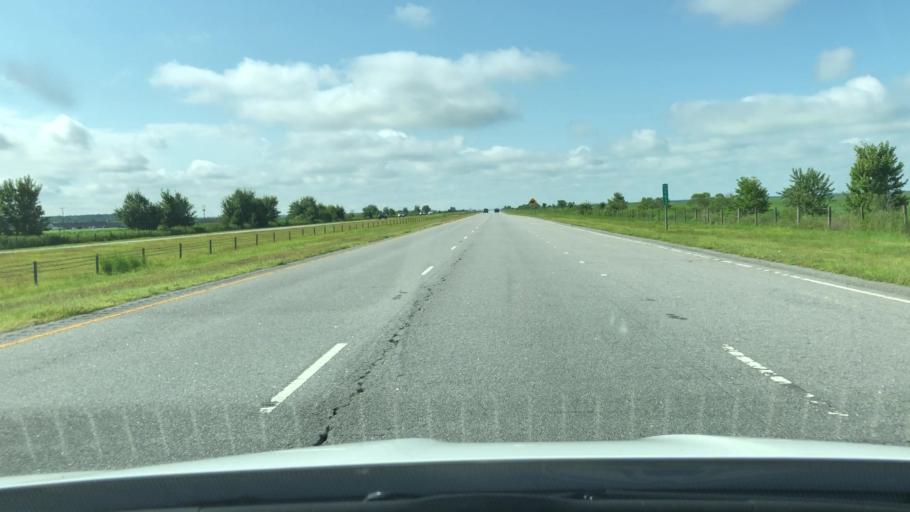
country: US
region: North Carolina
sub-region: Pasquotank County
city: Elizabeth City
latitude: 36.3617
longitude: -76.3159
